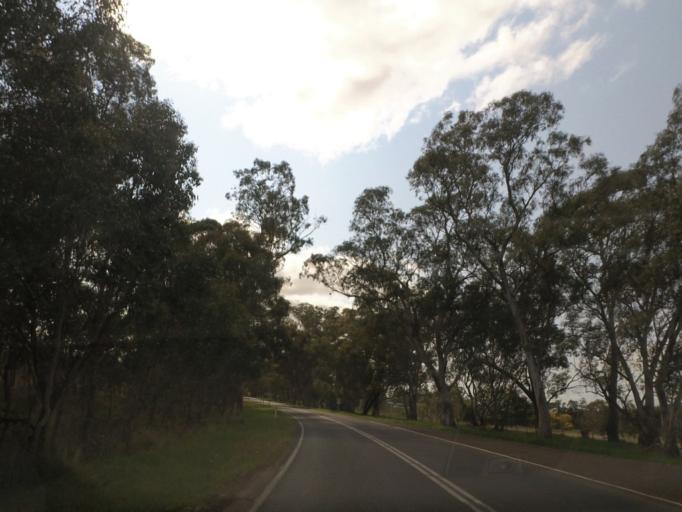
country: AU
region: Victoria
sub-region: Murrindindi
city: Kinglake West
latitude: -37.1069
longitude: 145.0944
